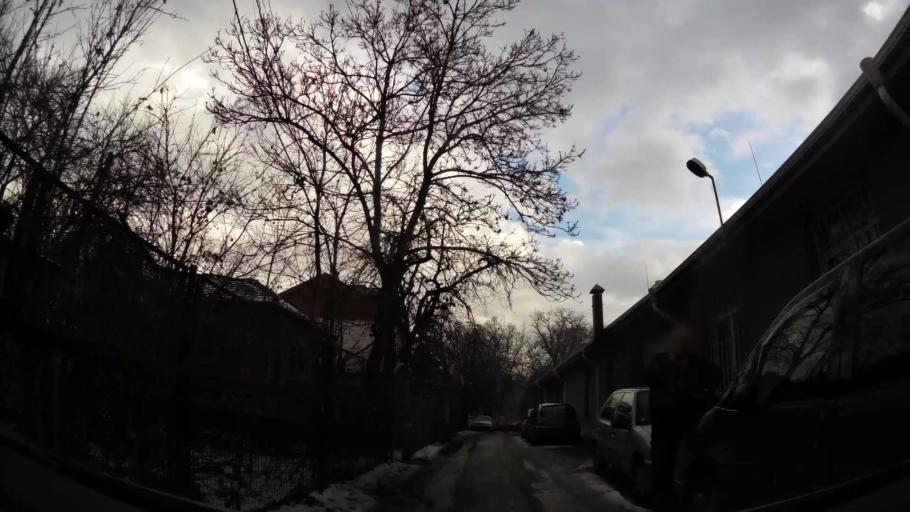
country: BG
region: Sofia-Capital
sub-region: Stolichna Obshtina
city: Sofia
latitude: 42.6949
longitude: 23.2922
